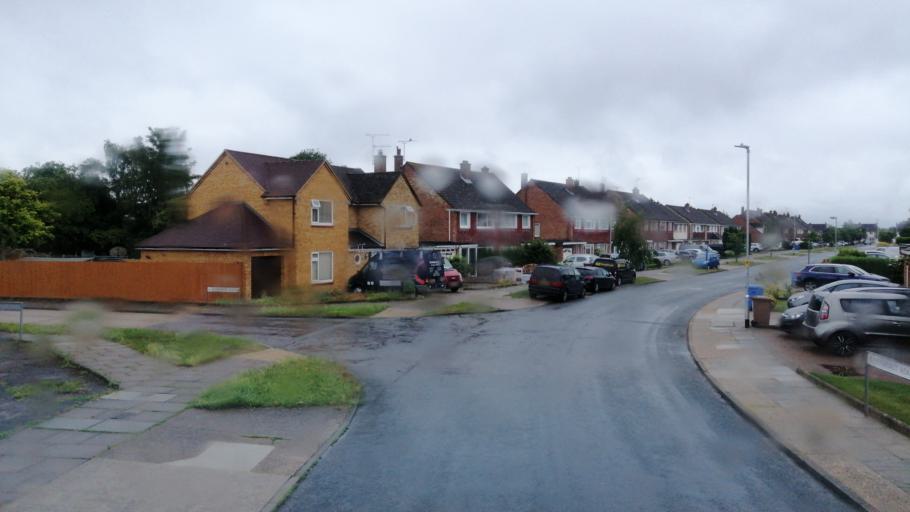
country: GB
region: England
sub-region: Suffolk
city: Kesgrave
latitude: 52.0484
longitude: 1.2049
